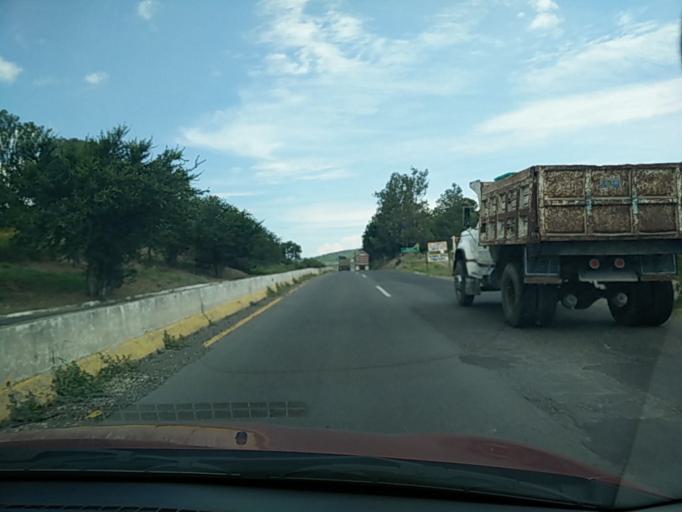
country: MX
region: Jalisco
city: Ixtlahuacan de los Membrillos
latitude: 20.3604
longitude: -103.1994
